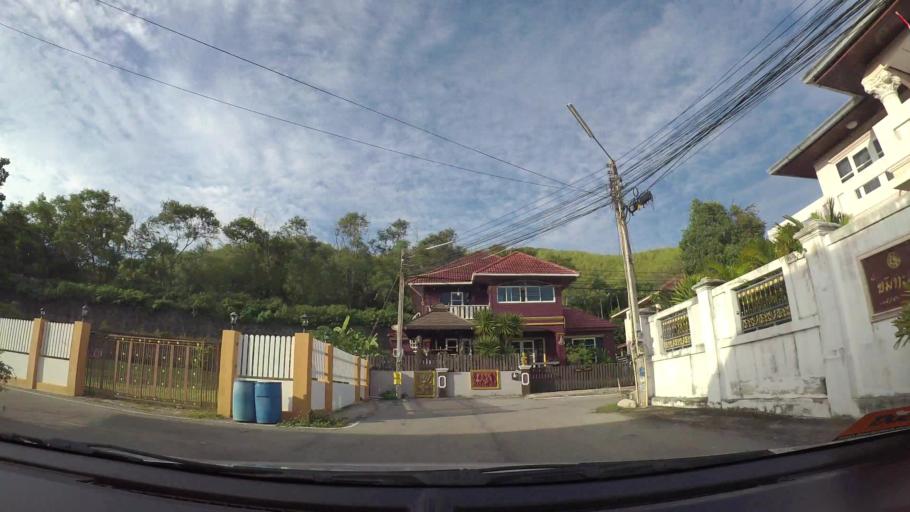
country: TH
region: Chon Buri
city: Sattahip
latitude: 12.6693
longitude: 100.9223
